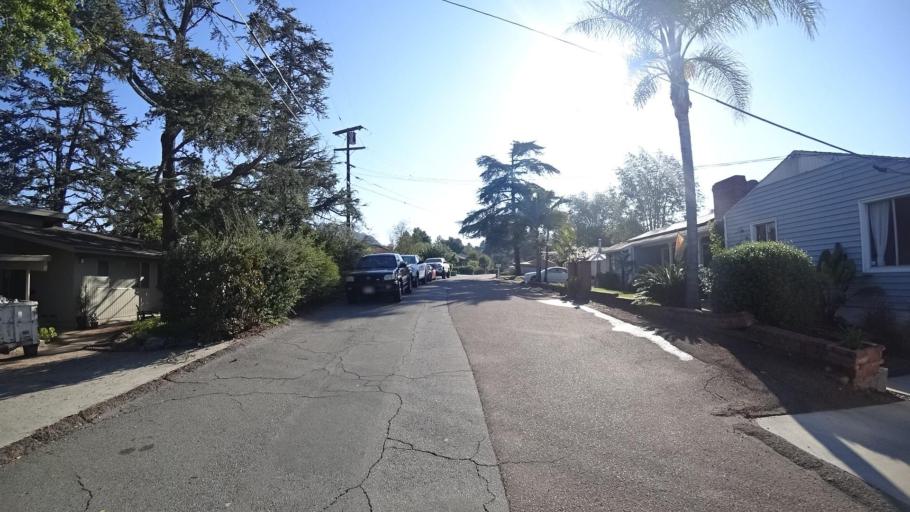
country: US
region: California
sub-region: San Diego County
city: Spring Valley
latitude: 32.7626
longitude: -116.9995
